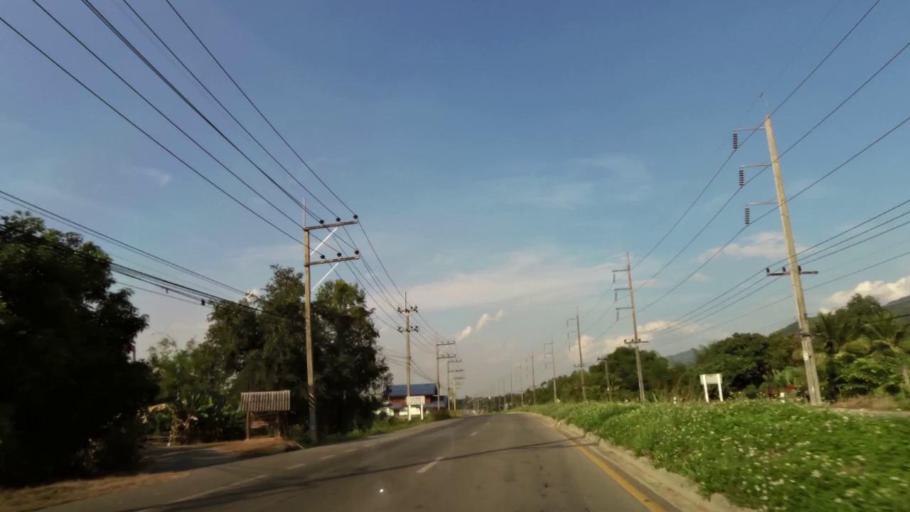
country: TH
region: Chiang Rai
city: Khun Tan
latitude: 19.8991
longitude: 100.2954
